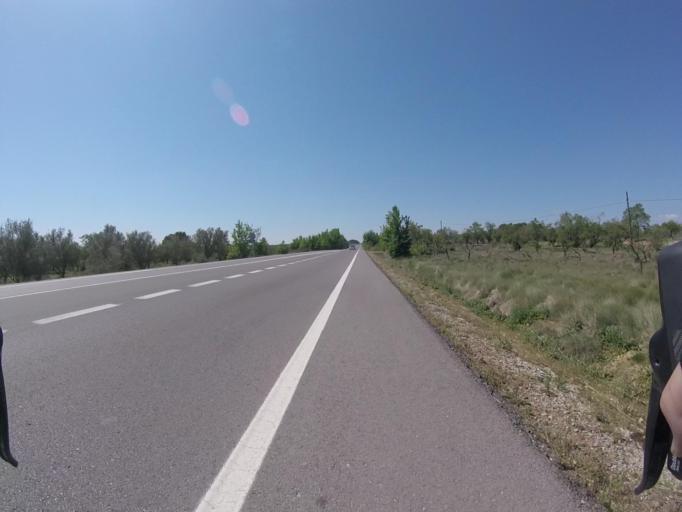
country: ES
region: Valencia
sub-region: Provincia de Castello
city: Benlloch
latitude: 40.2273
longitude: 0.0529
